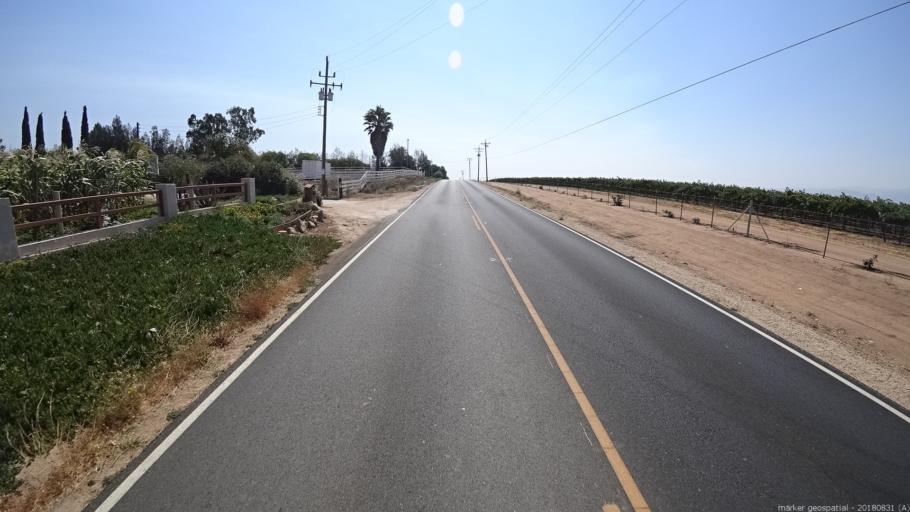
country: US
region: California
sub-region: Monterey County
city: Soledad
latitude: 36.4194
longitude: -121.2823
